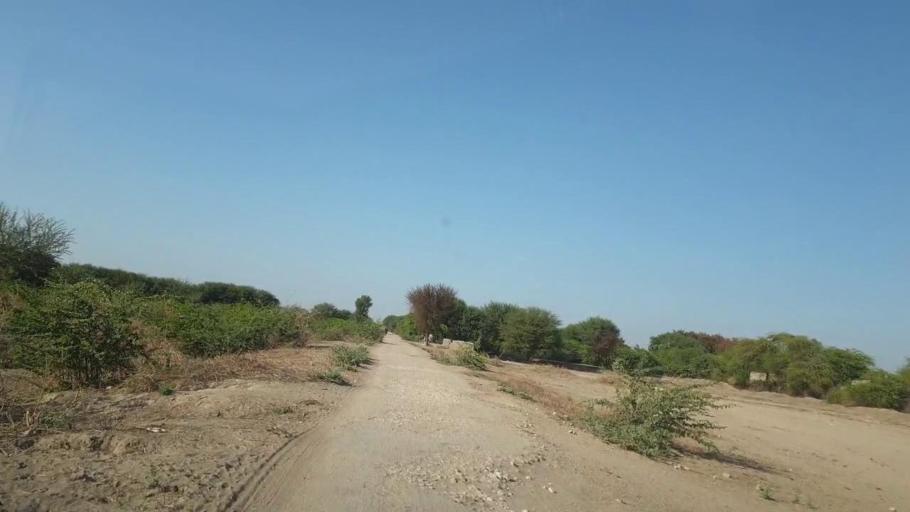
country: PK
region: Sindh
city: Kunri
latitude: 25.0491
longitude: 69.4420
